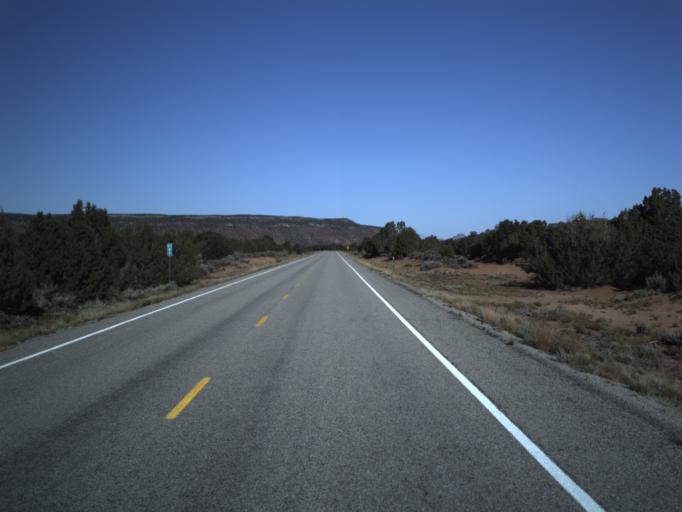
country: US
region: Utah
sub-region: San Juan County
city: Blanding
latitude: 37.5531
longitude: -109.9950
